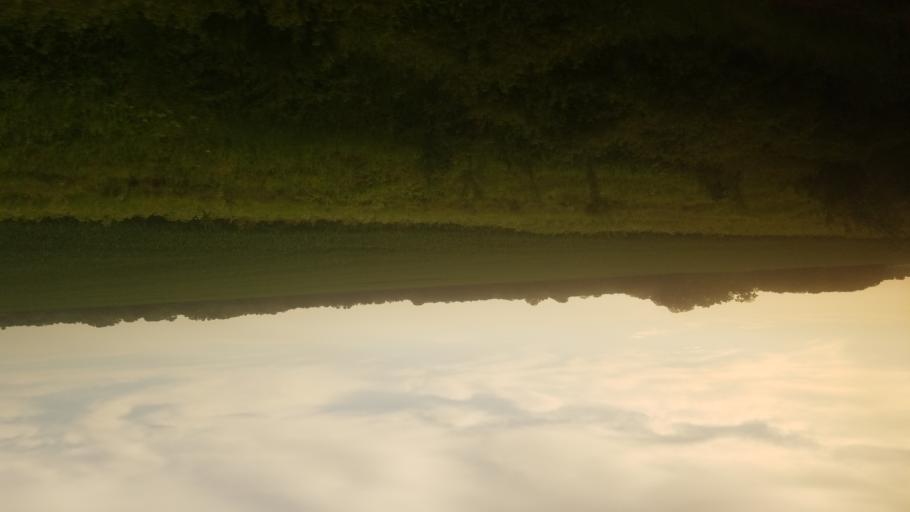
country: US
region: Kansas
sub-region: Osage County
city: Osage City
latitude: 38.5200
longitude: -95.9466
